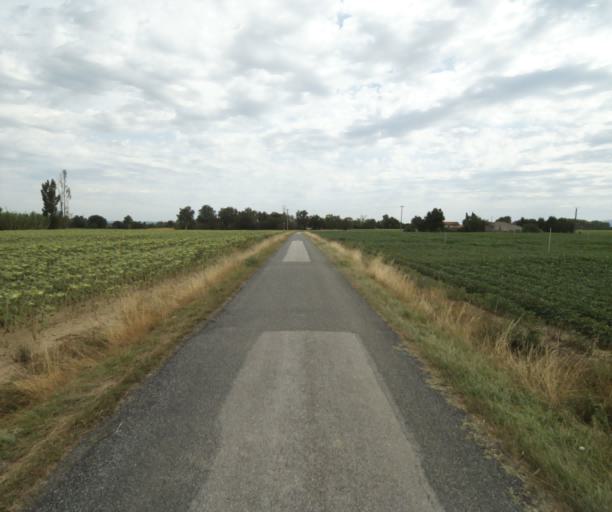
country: FR
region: Midi-Pyrenees
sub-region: Departement de la Haute-Garonne
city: Saint-Felix-Lauragais
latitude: 43.4448
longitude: 1.9310
